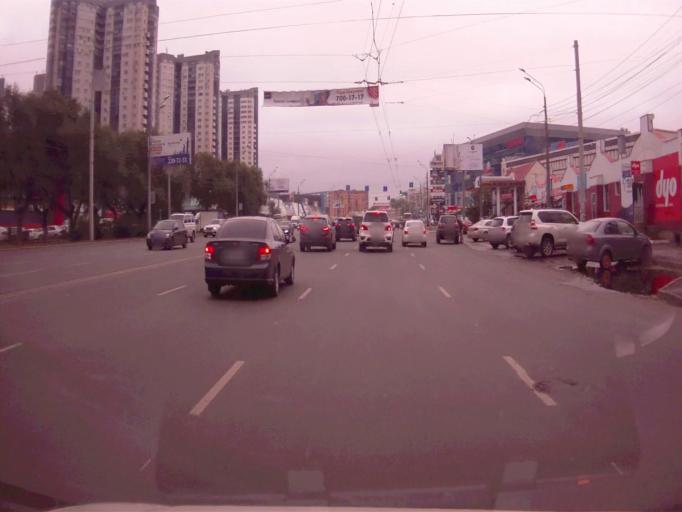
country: RU
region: Chelyabinsk
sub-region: Gorod Chelyabinsk
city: Chelyabinsk
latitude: 55.1695
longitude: 61.3747
